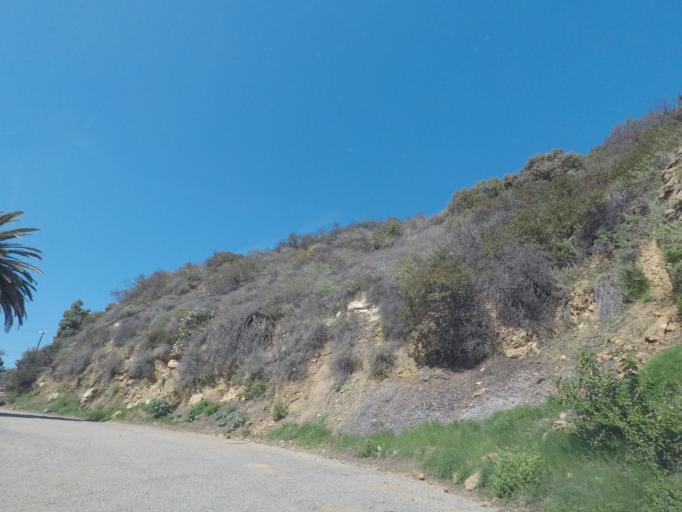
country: US
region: California
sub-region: Los Angeles County
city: Hollywood
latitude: 34.1164
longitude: -118.3295
